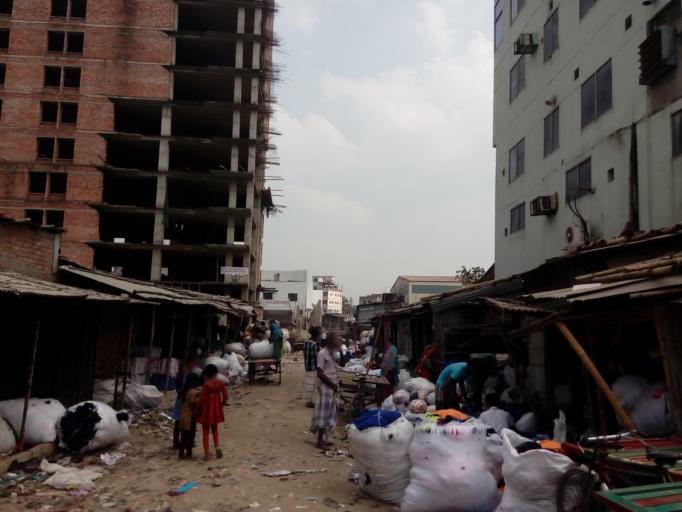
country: BD
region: Dhaka
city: Azimpur
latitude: 23.8116
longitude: 90.3741
